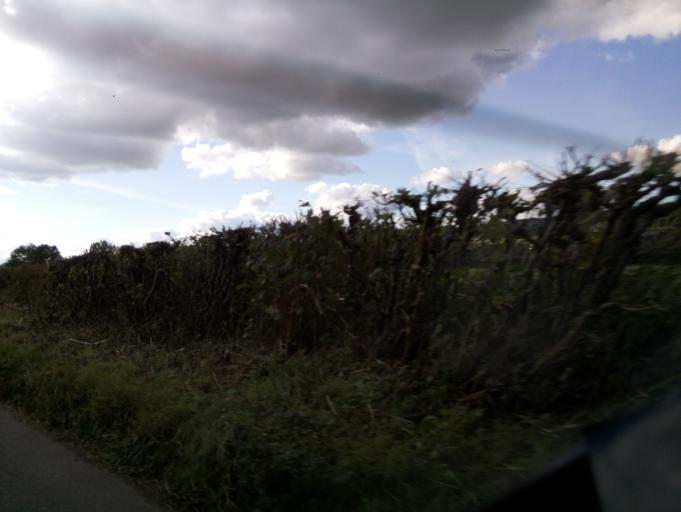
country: GB
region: Wales
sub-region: Sir Powys
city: Hay
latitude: 52.0597
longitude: -3.1616
